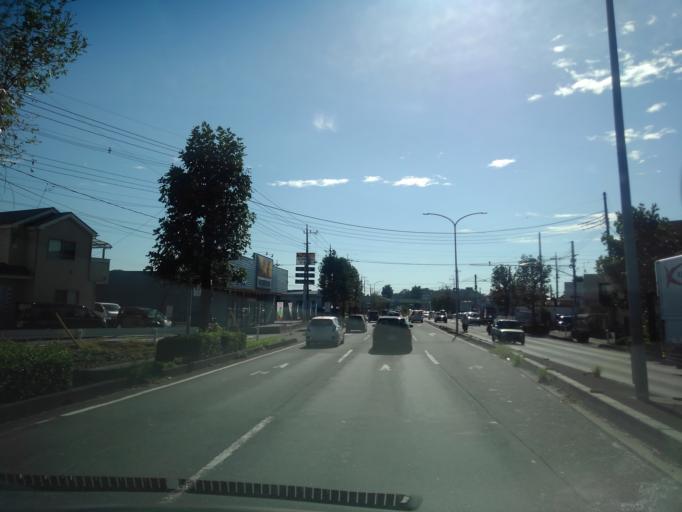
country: JP
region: Saitama
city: Sayama
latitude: 35.8140
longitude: 139.3950
